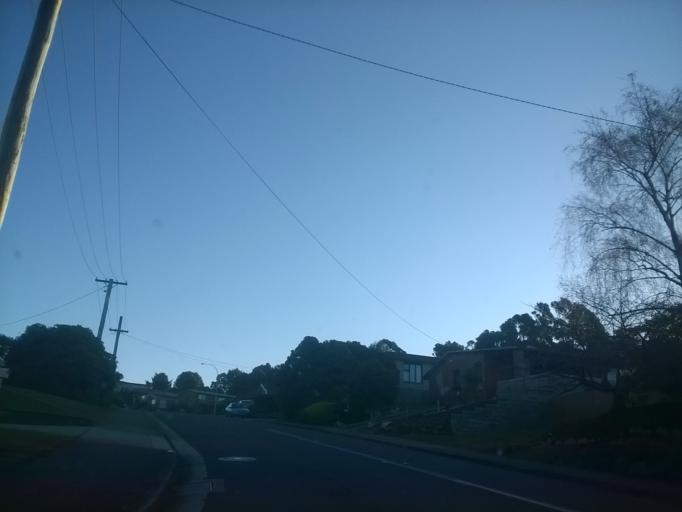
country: AU
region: Tasmania
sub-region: Burnie
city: Burnie
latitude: -41.0802
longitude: 145.9059
